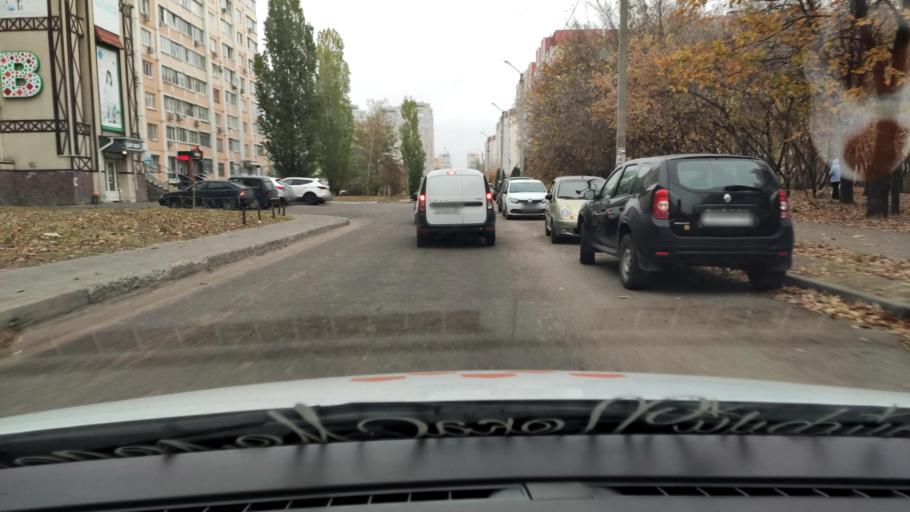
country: RU
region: Voronezj
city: Voronezh
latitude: 51.7077
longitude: 39.1873
